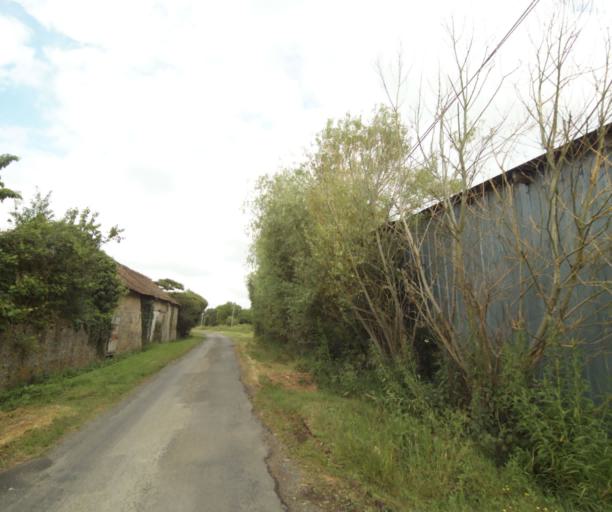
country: FR
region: Pays de la Loire
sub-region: Departement de la Sarthe
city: Solesmes
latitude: 47.8305
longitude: -0.2860
